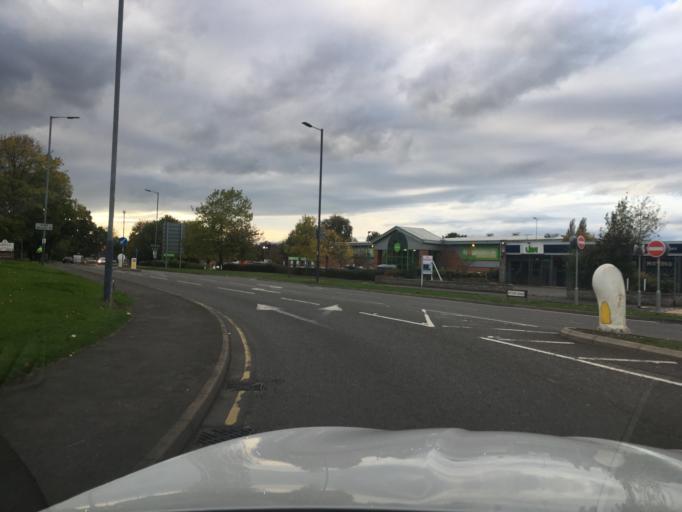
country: GB
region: England
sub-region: Warwickshire
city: Royal Leamington Spa
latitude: 52.2830
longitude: -1.5476
